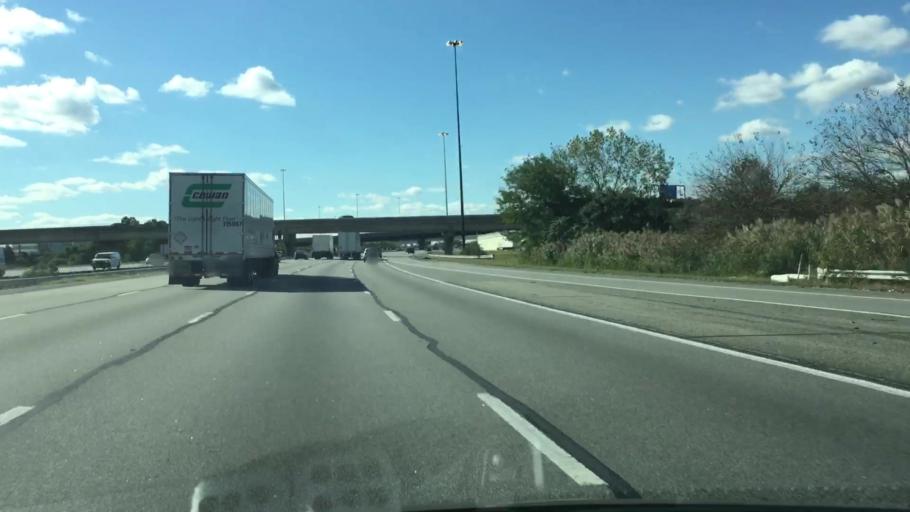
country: US
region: Pennsylvania
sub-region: Delaware County
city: Colwyn
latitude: 39.8780
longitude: -75.2488
